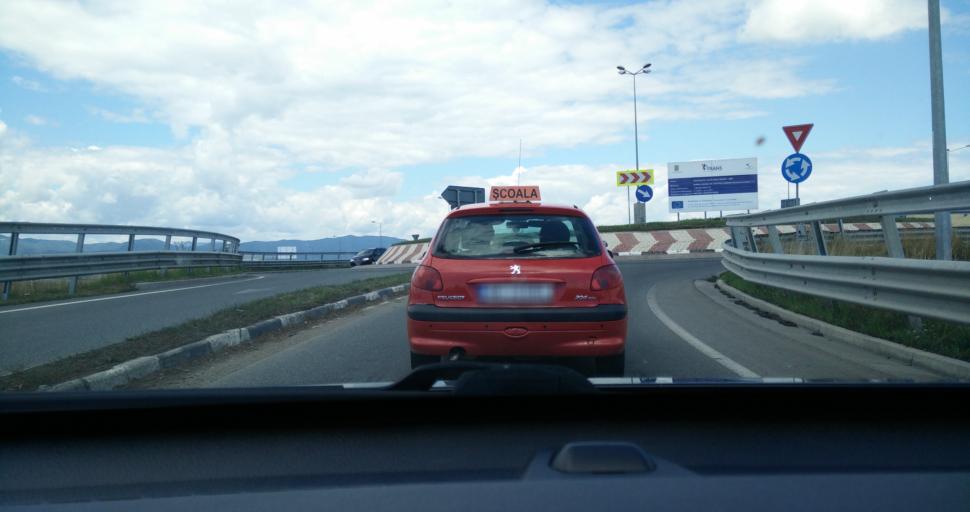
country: RO
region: Alba
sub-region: Municipiul Sebes
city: Lancram
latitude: 45.9737
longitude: 23.5565
